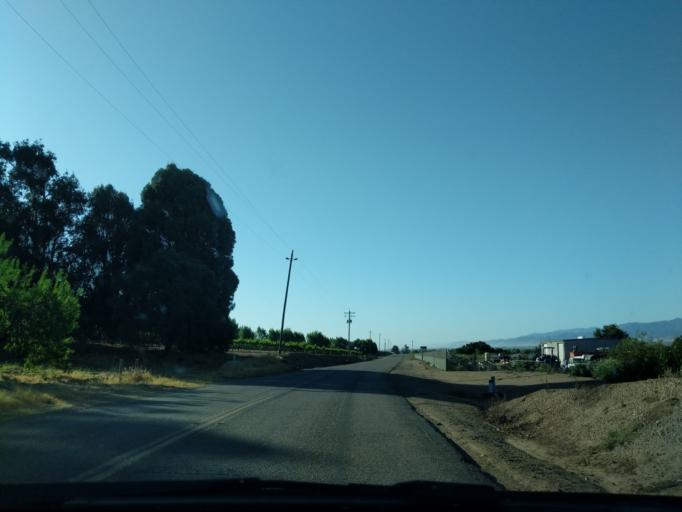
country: US
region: California
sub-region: Monterey County
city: Gonzales
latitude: 36.4836
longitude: -121.4884
